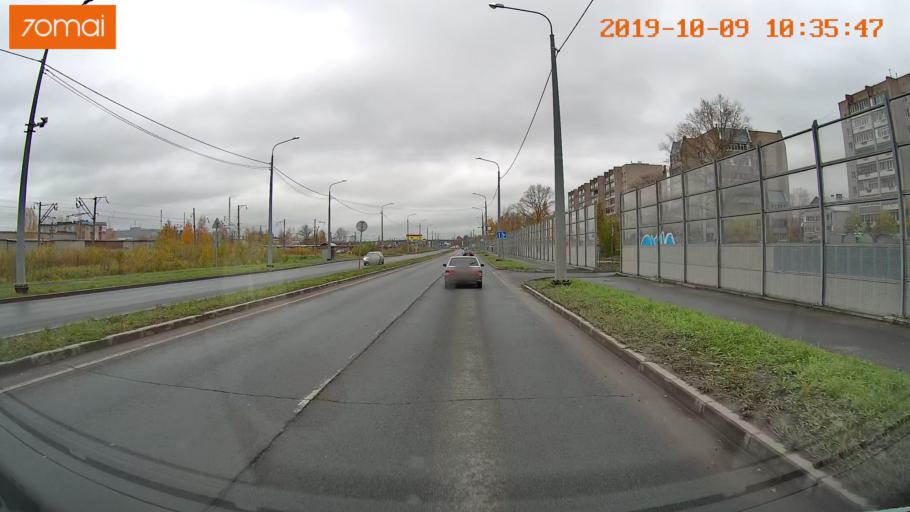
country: RU
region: Vologda
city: Vologda
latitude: 59.2284
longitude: 39.8617
